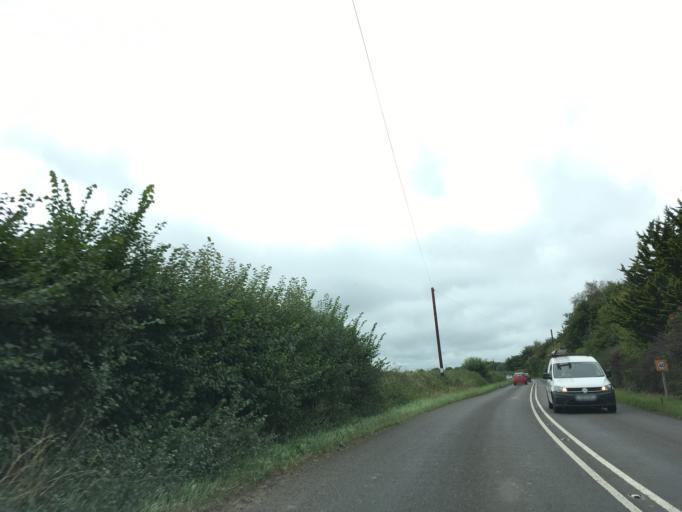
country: GB
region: England
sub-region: Bath and North East Somerset
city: Saltford
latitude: 51.3852
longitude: -2.4807
